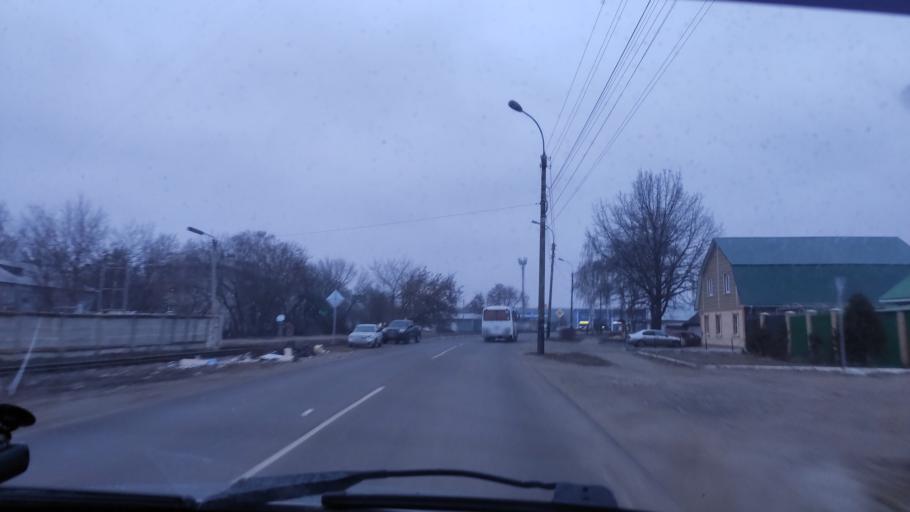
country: RU
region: Tambov
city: Pokrovo-Prigorodnoye
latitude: 52.7194
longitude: 41.3881
